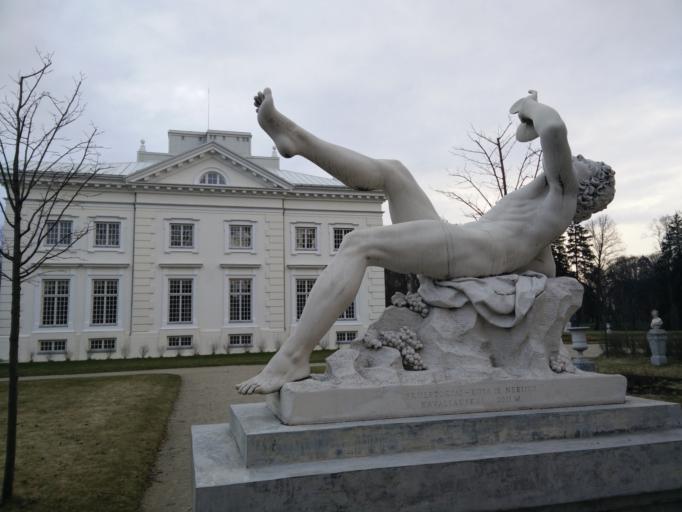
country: LT
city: Trakai
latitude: 54.6592
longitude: 24.9441
